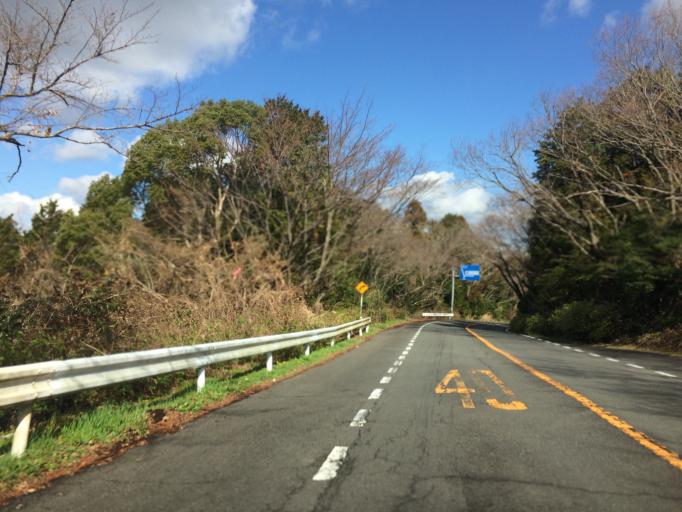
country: JP
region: Shizuoka
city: Shizuoka-shi
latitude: 34.9759
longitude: 138.4472
